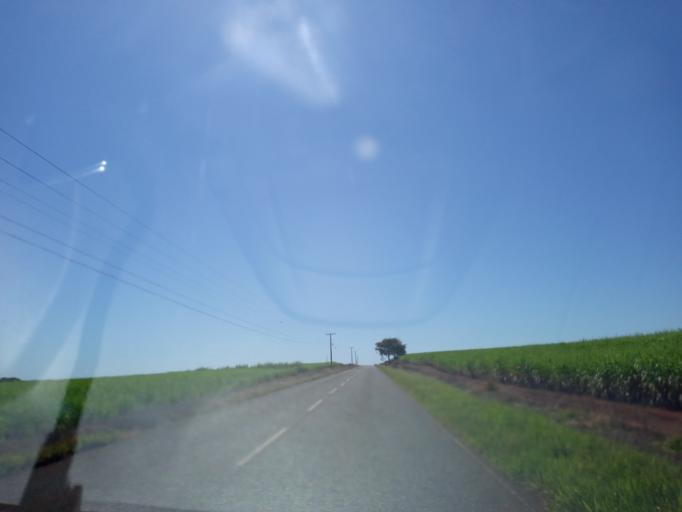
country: BR
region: Goias
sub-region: Itumbiara
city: Itumbiara
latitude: -18.4251
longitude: -49.1701
